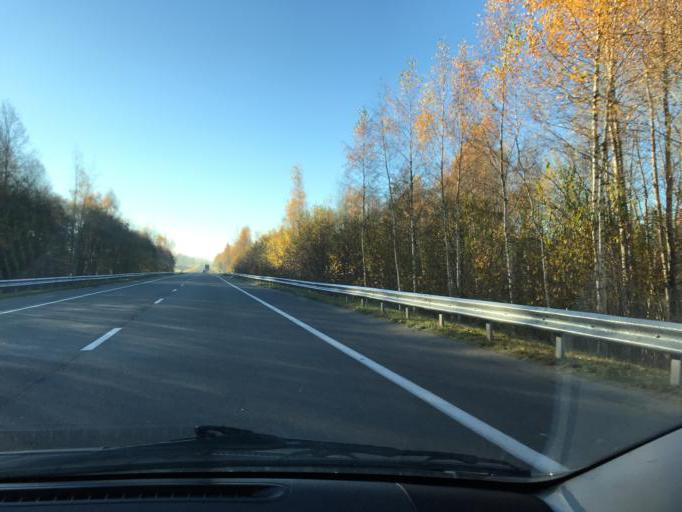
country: BY
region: Vitebsk
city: Vitebsk
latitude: 55.0107
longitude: 30.3316
